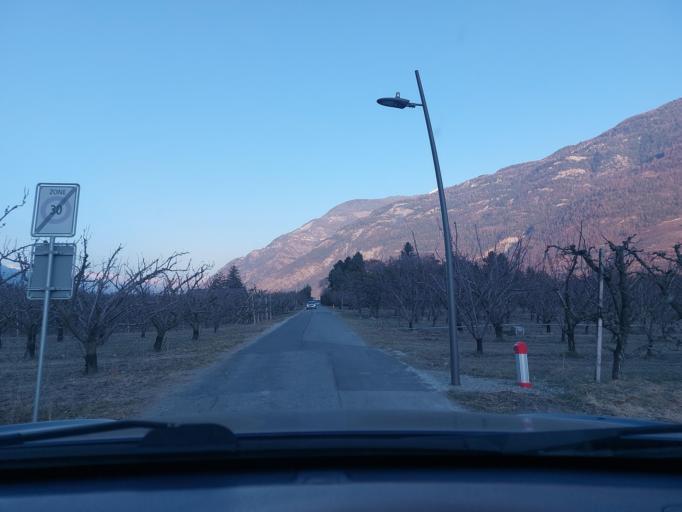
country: CH
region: Valais
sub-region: Martigny District
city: Saxon
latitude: 46.1558
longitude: 7.1795
